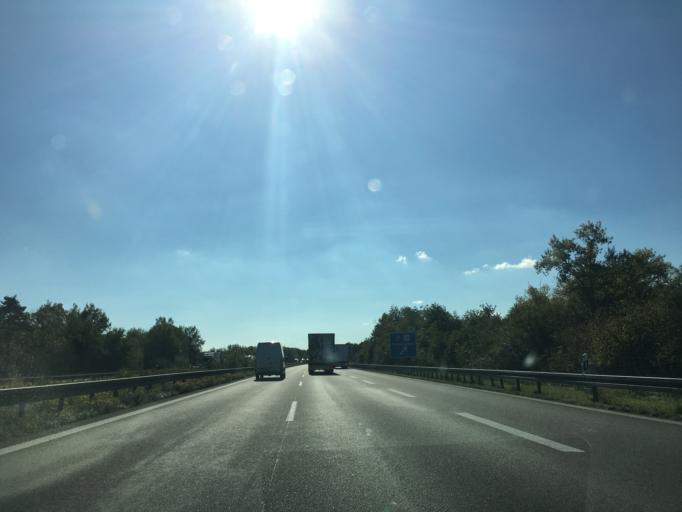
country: DE
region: Baden-Wuerttemberg
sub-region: Freiburg Region
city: Neuenburg am Rhein
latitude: 47.8335
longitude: 7.5643
